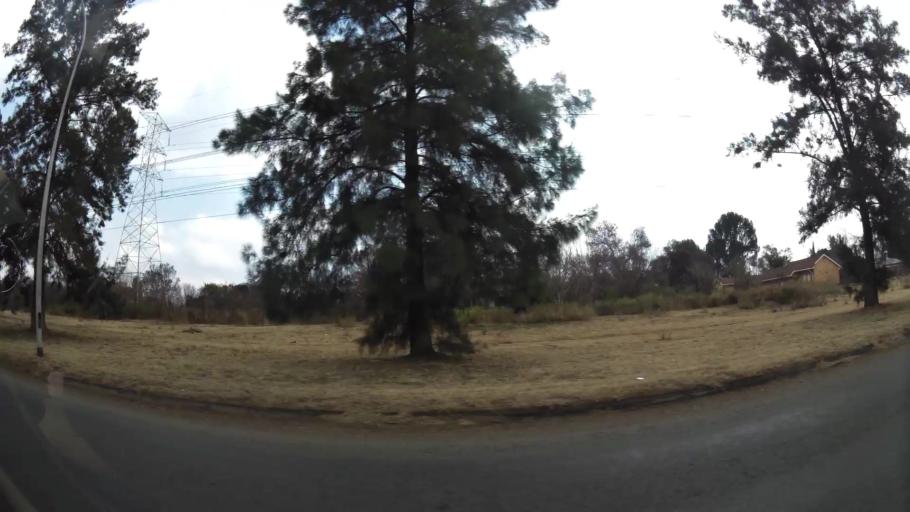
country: ZA
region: Gauteng
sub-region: Sedibeng District Municipality
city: Vereeniging
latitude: -26.6773
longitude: 27.9377
